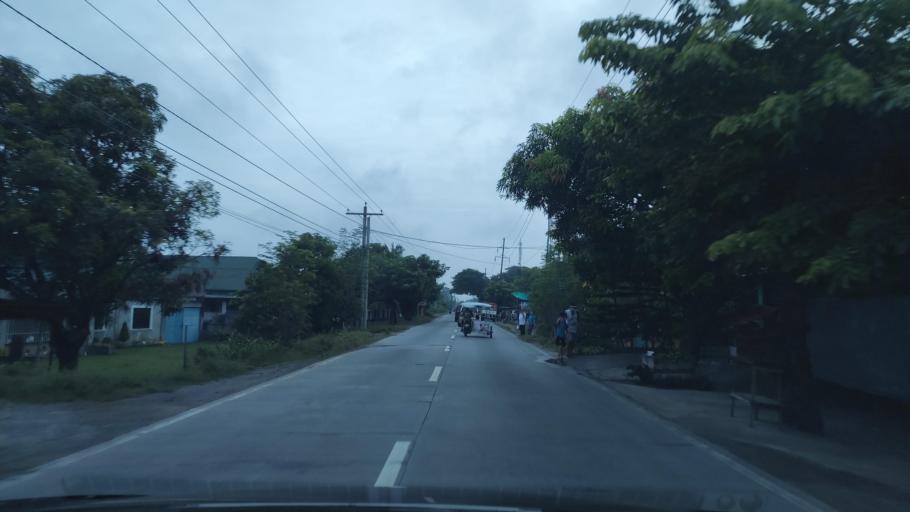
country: PH
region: Central Luzon
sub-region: Province of Pampanga
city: Laug
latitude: 15.0474
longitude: 120.7513
